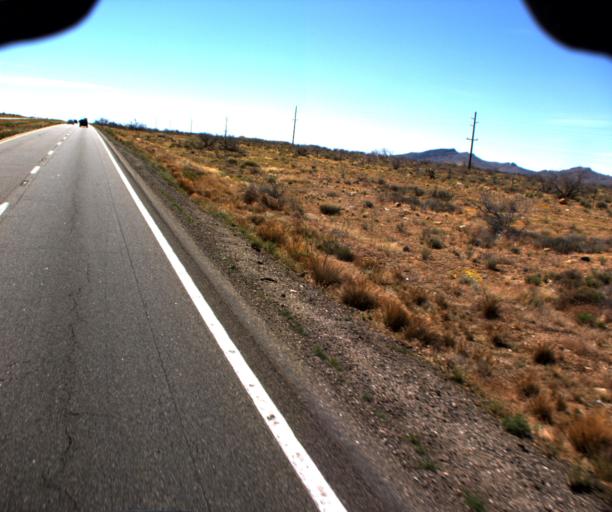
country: US
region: Arizona
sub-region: Mohave County
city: Dolan Springs
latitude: 35.4299
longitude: -114.2835
